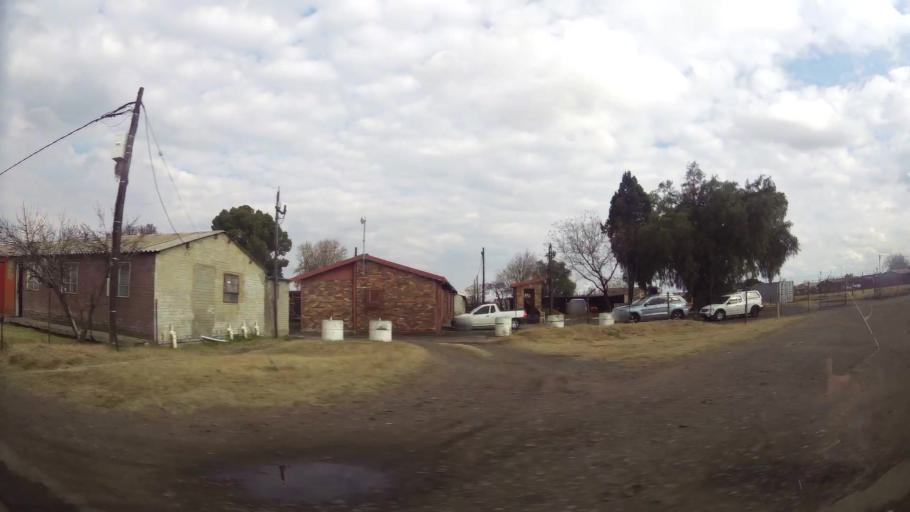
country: ZA
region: Orange Free State
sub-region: Fezile Dabi District Municipality
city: Sasolburg
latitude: -26.8397
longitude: 27.8517
